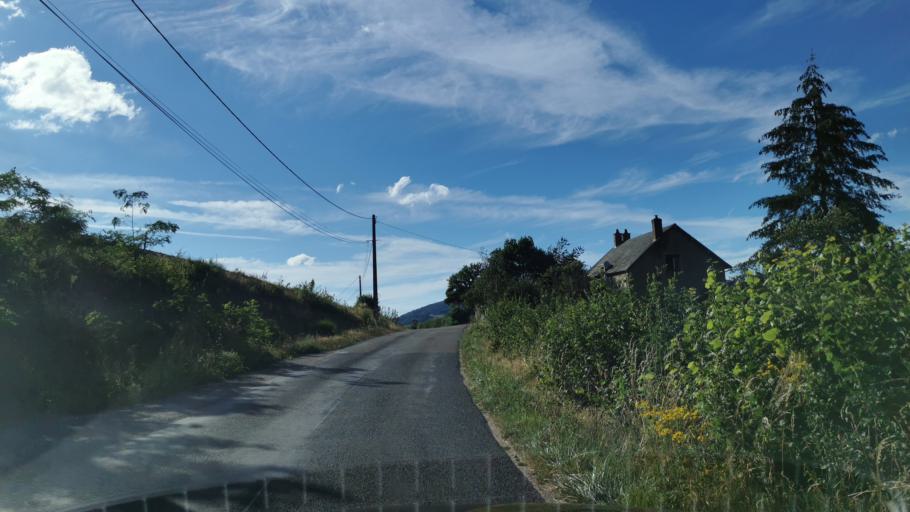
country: FR
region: Bourgogne
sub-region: Departement de Saone-et-Loire
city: Marmagne
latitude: 46.8455
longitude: 4.3231
